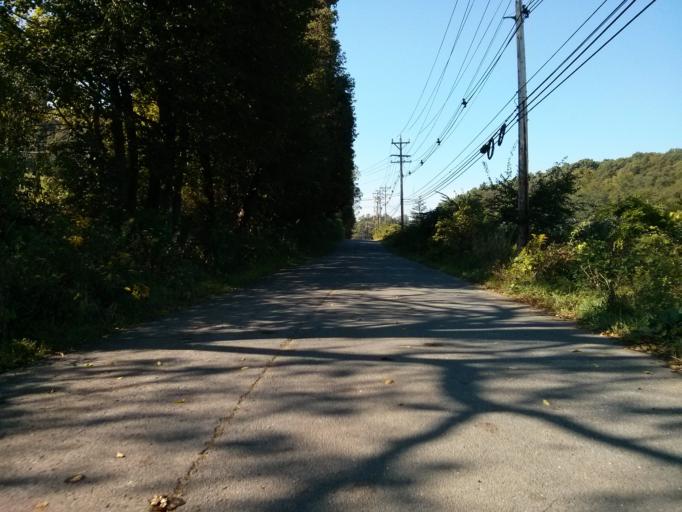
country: US
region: Pennsylvania
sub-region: Centre County
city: State College
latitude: 40.8198
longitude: -77.8711
